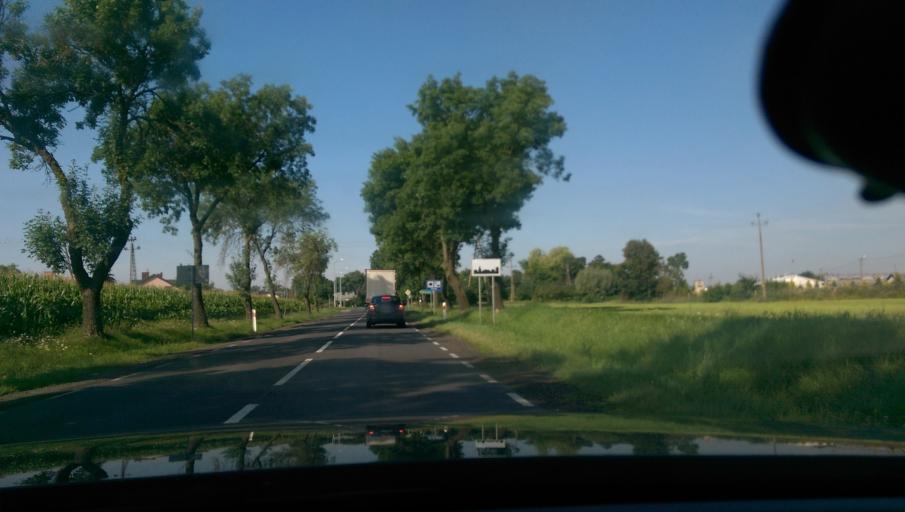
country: PL
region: Masovian Voivodeship
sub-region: Powiat plonski
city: Plonsk
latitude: 52.6350
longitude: 20.3912
